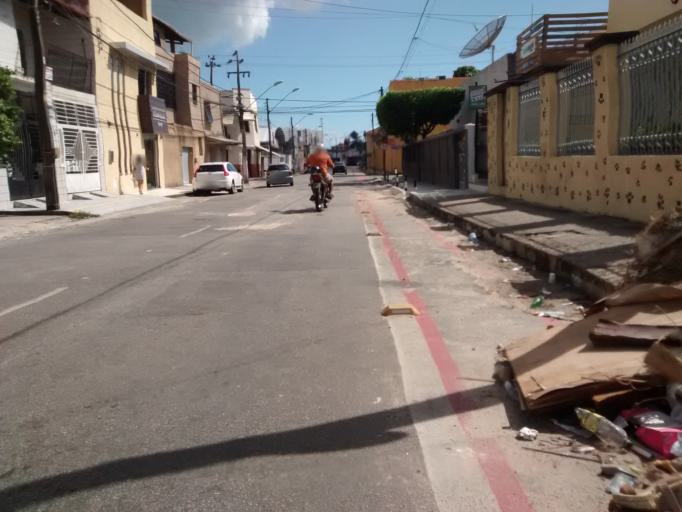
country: BR
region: Ceara
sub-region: Fortaleza
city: Fortaleza
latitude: -3.7346
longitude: -38.5507
